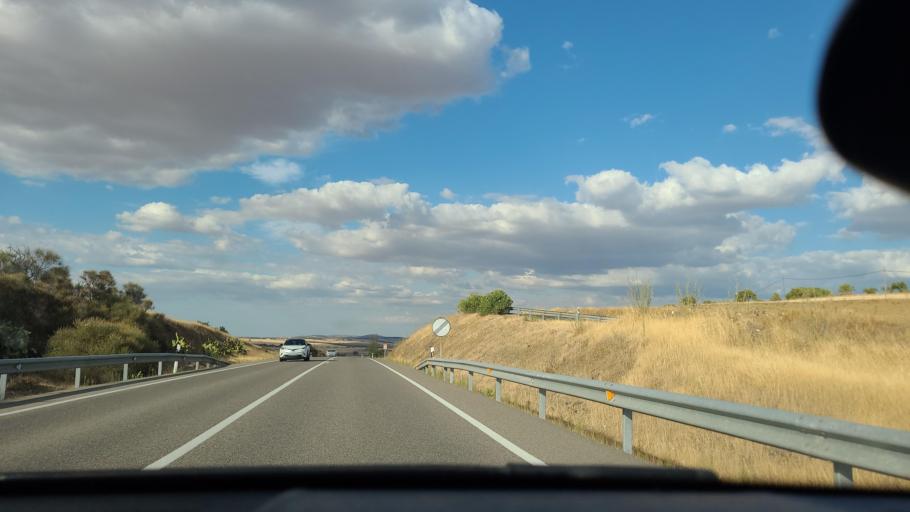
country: ES
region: Andalusia
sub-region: Province of Cordoba
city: Fuente Obejuna
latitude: 38.2665
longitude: -5.4352
